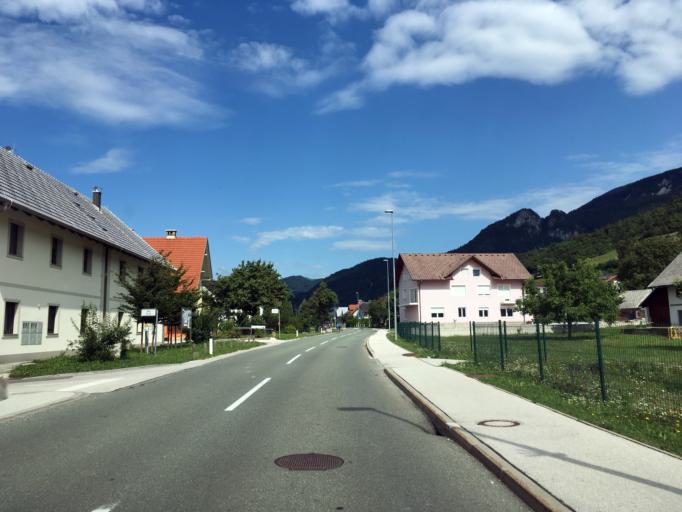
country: SI
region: Zirovnica
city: Zirovnica
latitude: 46.3994
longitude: 14.1431
